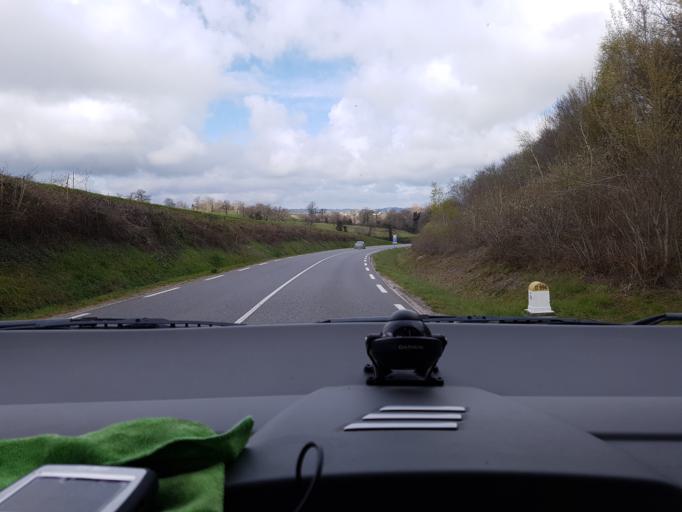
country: FR
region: Midi-Pyrenees
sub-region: Departement de l'Aveyron
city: Colombies
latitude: 44.4005
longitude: 2.3494
